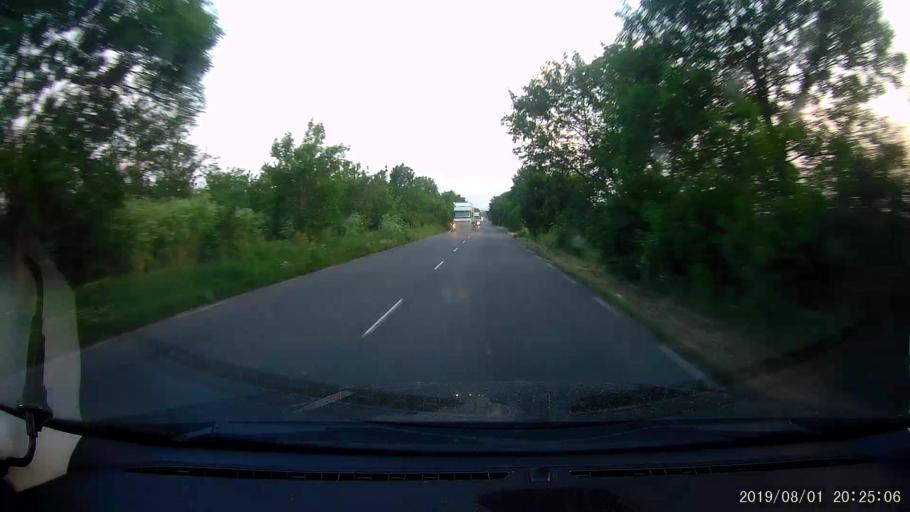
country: BG
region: Yambol
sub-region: Obshtina Elkhovo
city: Elkhovo
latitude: 42.2209
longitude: 26.5895
